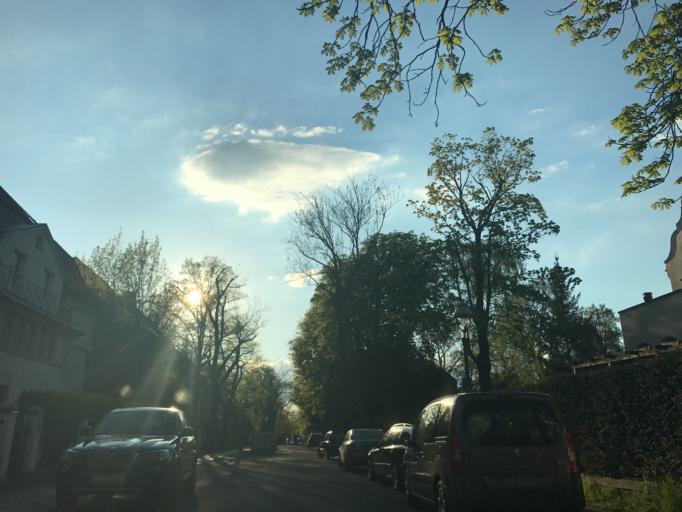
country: DE
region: Berlin
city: Westend
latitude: 52.5149
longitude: 13.2729
